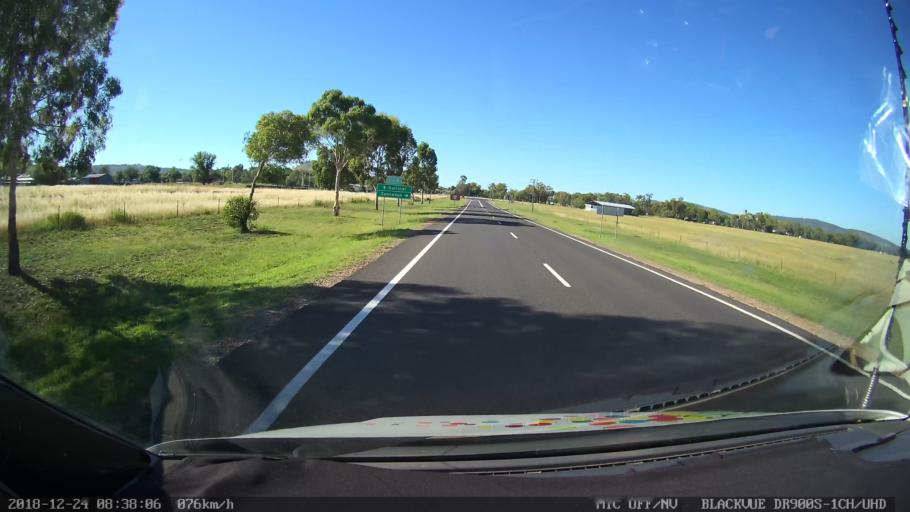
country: AU
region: New South Wales
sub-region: Liverpool Plains
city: Quirindi
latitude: -31.3378
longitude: 150.6477
